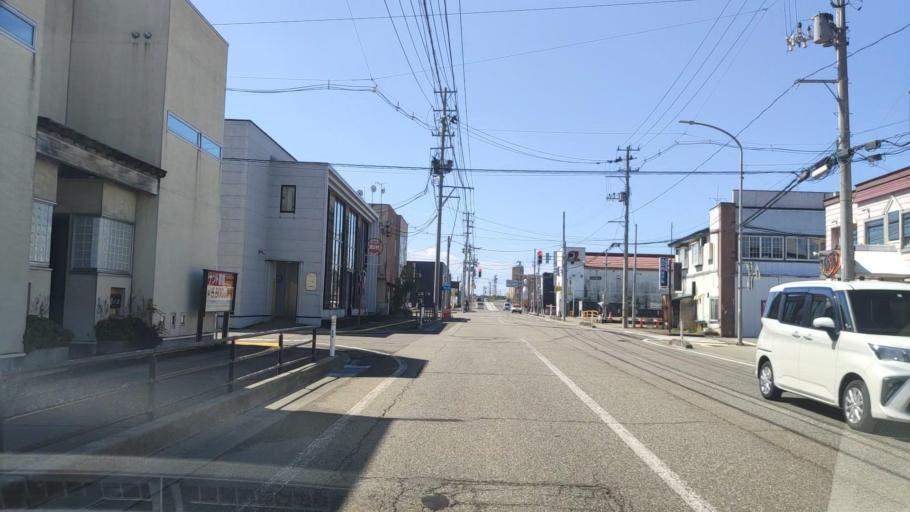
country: JP
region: Akita
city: Omagari
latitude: 39.4631
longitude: 140.4763
